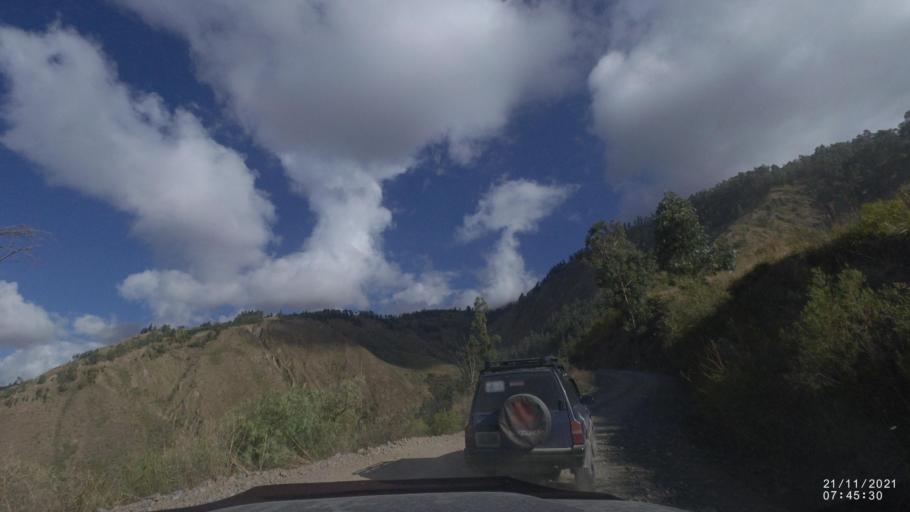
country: BO
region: Cochabamba
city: Cochabamba
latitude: -17.3153
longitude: -66.2192
